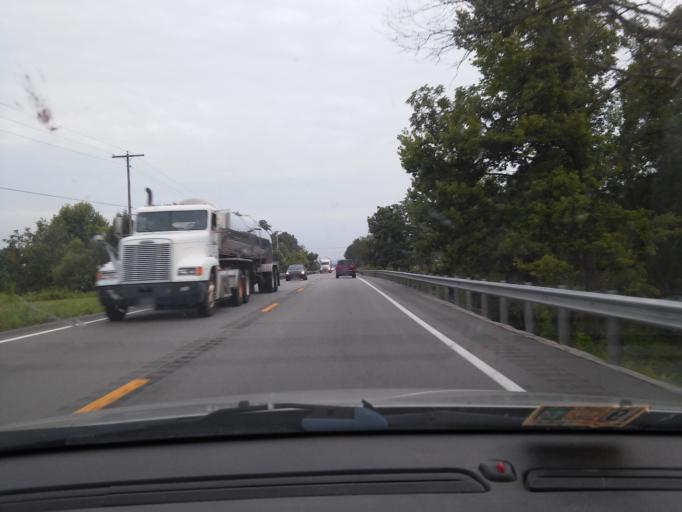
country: US
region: West Virginia
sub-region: Putnam County
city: Buffalo
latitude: 38.6761
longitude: -81.9657
